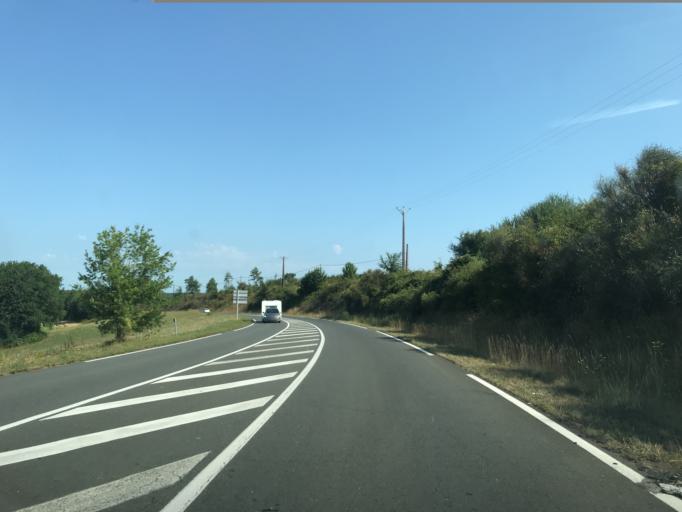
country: FR
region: Aquitaine
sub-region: Departement de la Dordogne
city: Montignac
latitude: 45.0419
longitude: 1.2289
